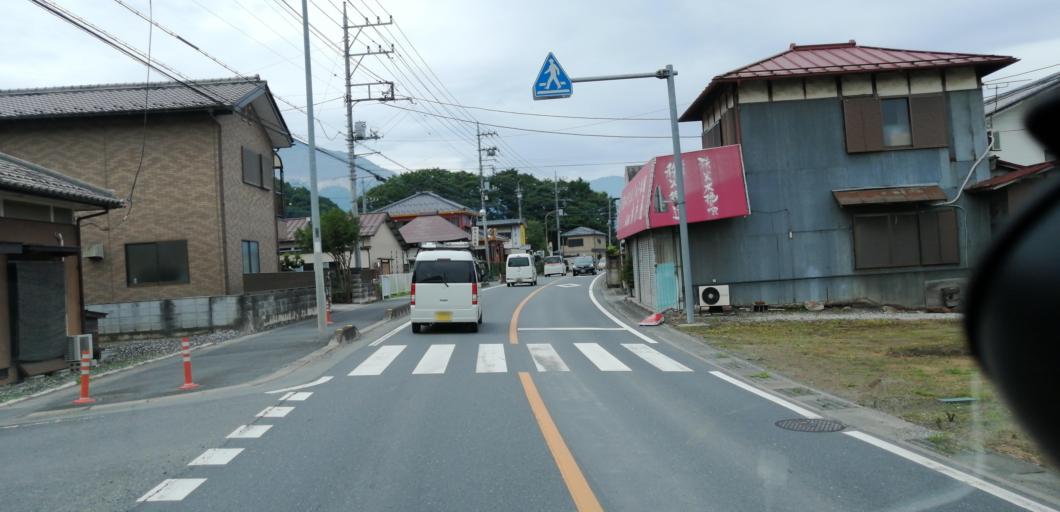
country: JP
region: Saitama
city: Chichibu
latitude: 36.0082
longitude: 139.1115
